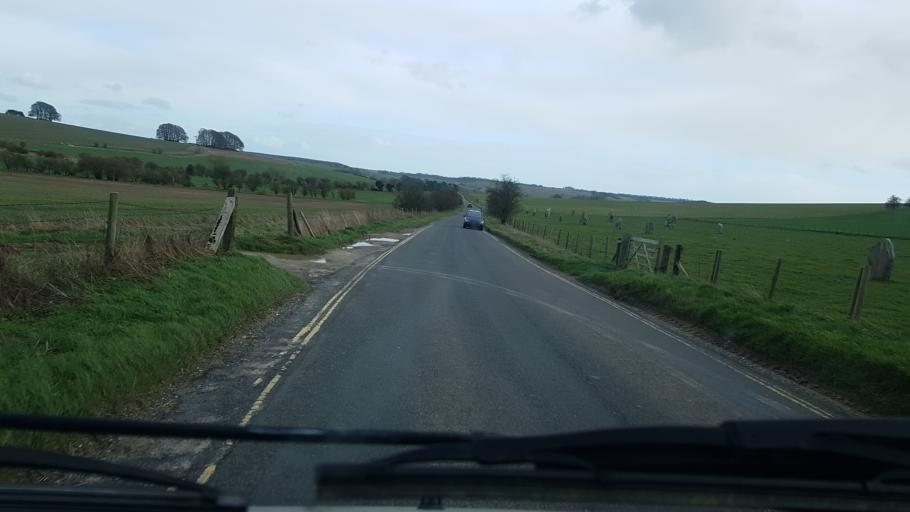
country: GB
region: England
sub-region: Wiltshire
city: Avebury
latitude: 51.4229
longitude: -1.8476
